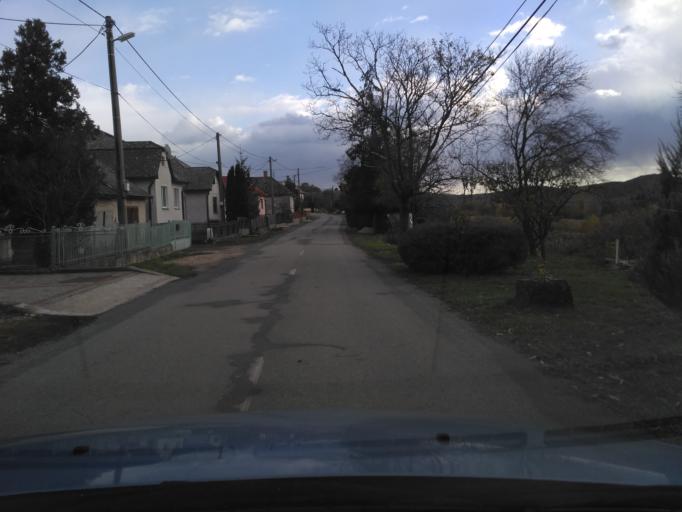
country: HU
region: Borsod-Abauj-Zemplen
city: Satoraljaujhely
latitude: 48.4384
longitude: 21.7345
